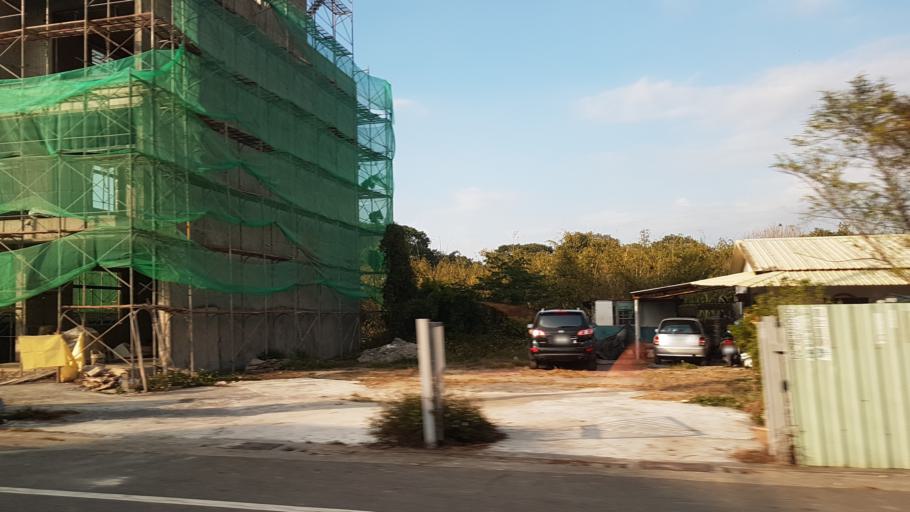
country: TW
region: Taiwan
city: Xinying
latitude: 23.3463
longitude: 120.4228
